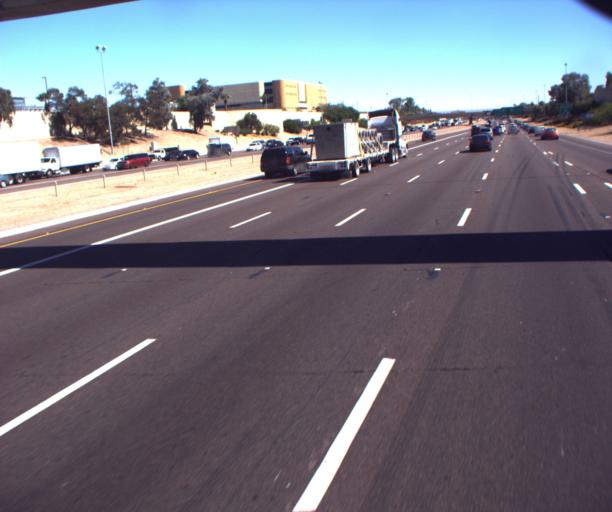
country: US
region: Arizona
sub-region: Maricopa County
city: Phoenix
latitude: 33.4617
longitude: -112.0611
